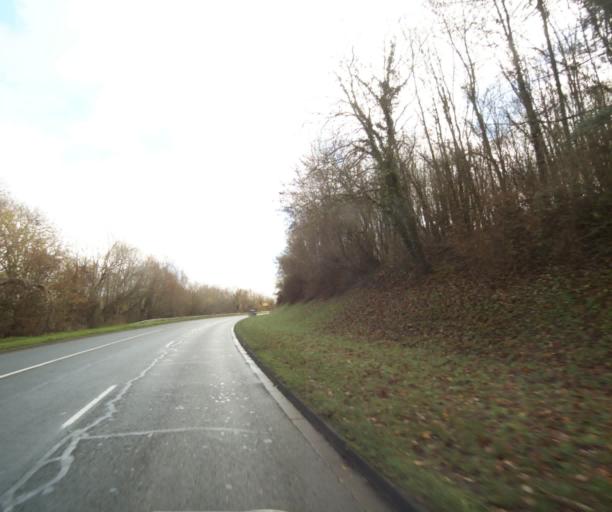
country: FR
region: Ile-de-France
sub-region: Departement des Yvelines
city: Meulan-en-Yvelines
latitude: 49.0154
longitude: 1.9204
